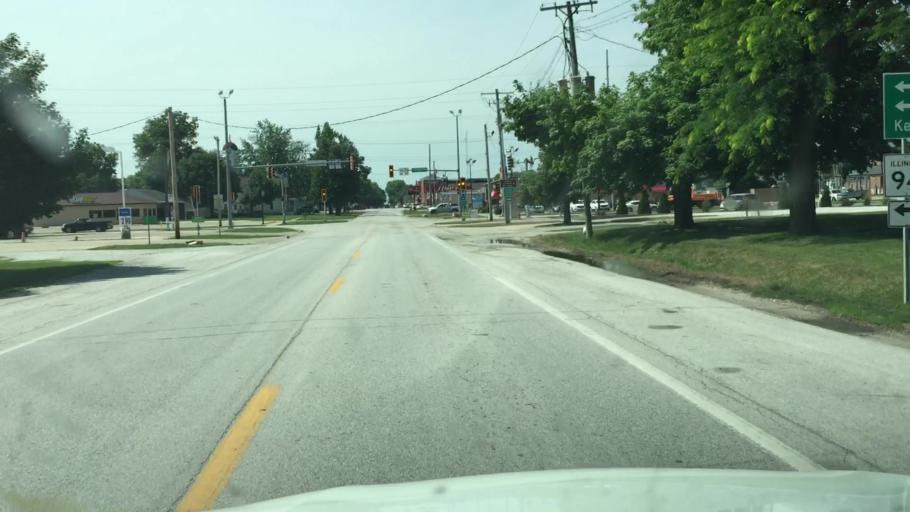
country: US
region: Illinois
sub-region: Hancock County
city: Carthage
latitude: 40.4172
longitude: -91.1362
